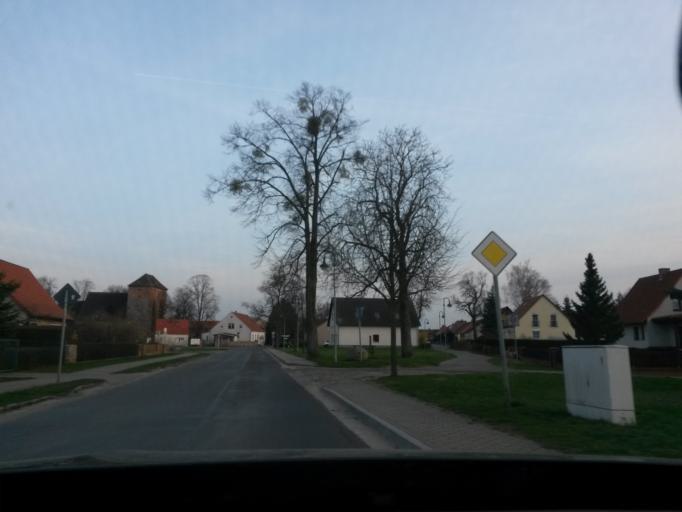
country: DE
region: Brandenburg
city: Protzel
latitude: 52.5918
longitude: 13.9493
